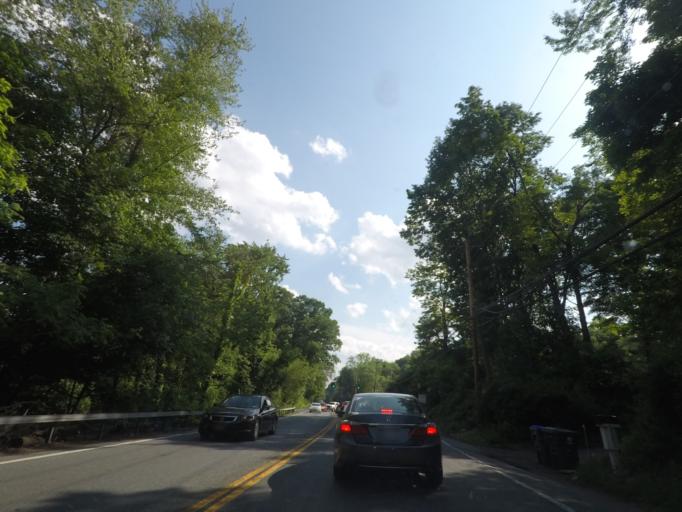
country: US
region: New York
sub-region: Orange County
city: Balmville
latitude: 41.5289
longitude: -74.0182
